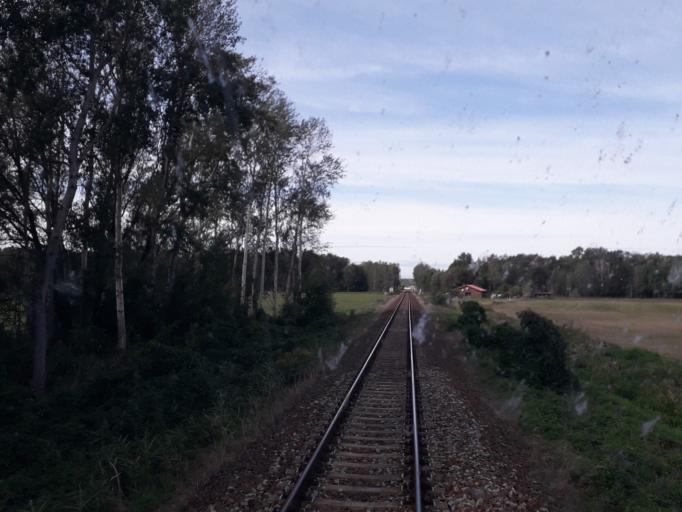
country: DE
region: Brandenburg
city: Kremmen
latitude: 52.7839
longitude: 13.0394
